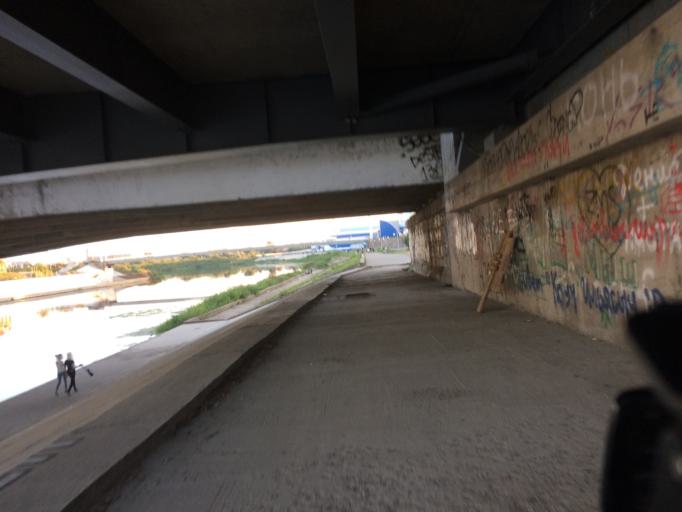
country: RU
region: Mariy-El
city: Yoshkar-Ola
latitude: 56.6288
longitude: 47.8986
